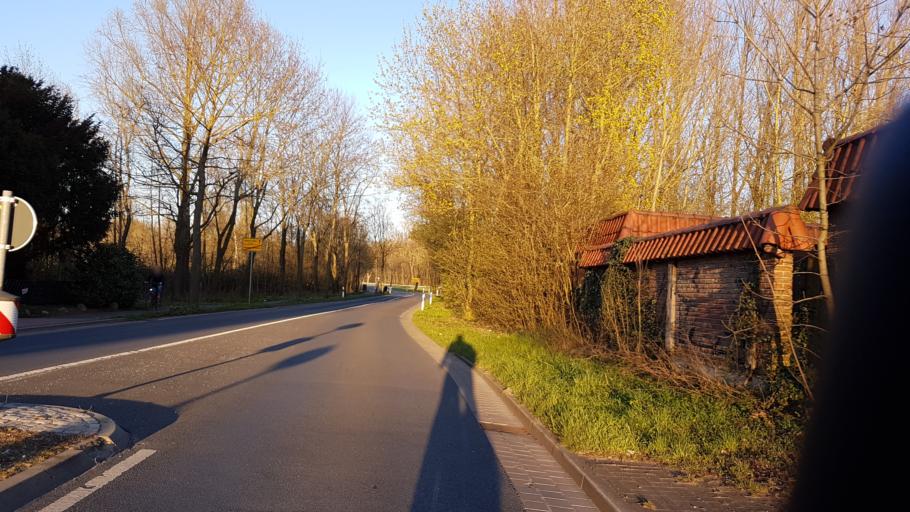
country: DE
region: Lower Saxony
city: Hemmingen
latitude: 52.3194
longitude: 9.7513
